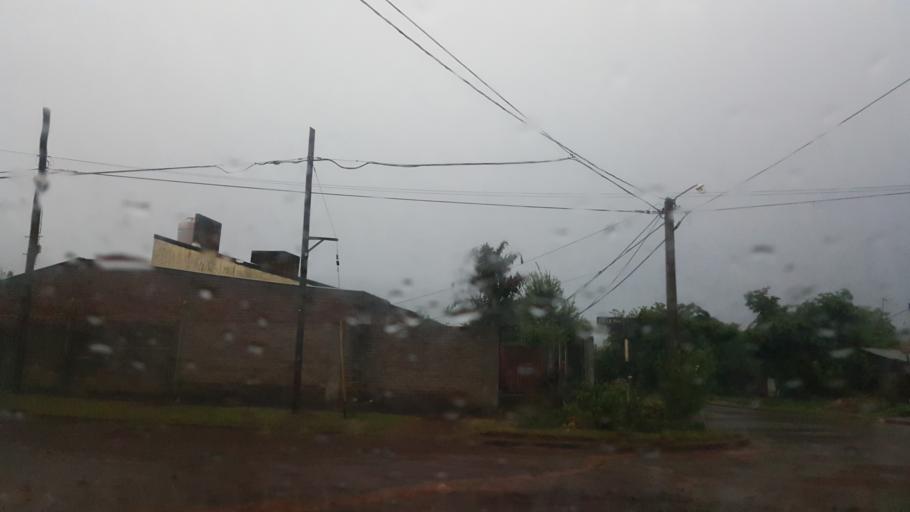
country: AR
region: Misiones
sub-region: Departamento de Capital
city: Posadas
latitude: -27.4118
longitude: -55.9423
